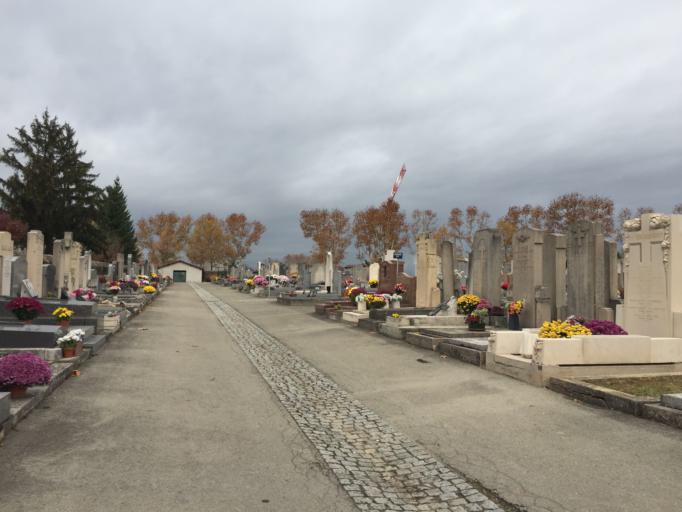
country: FR
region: Rhone-Alpes
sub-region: Departement du Rhone
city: Gleize
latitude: 45.9960
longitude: 4.7124
